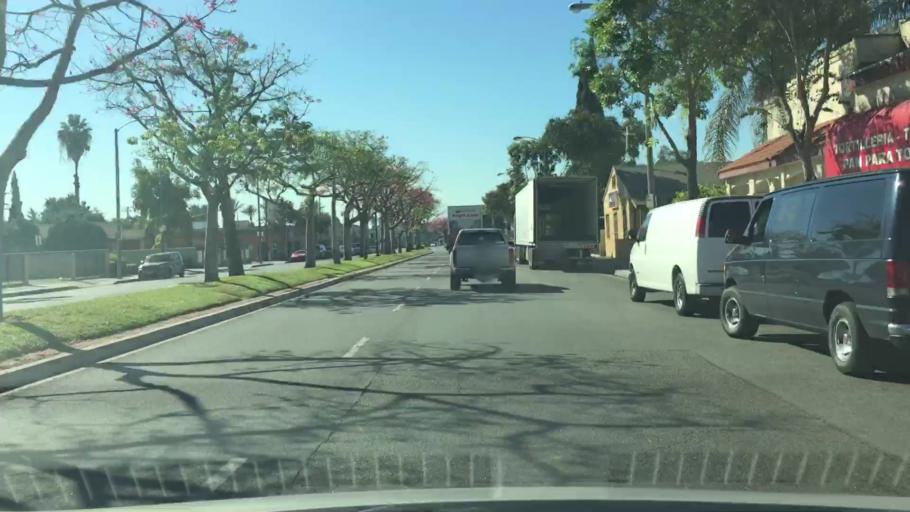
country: US
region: California
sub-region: Los Angeles County
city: Bell Gardens
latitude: 33.9735
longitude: -118.1640
